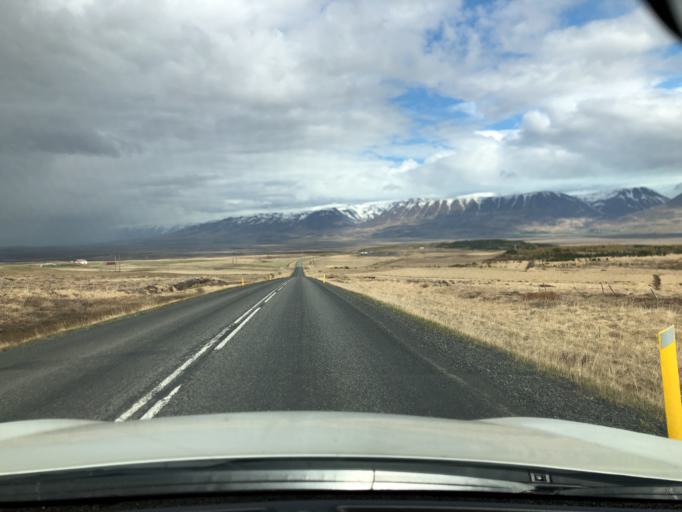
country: IS
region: Northwest
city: Saudarkrokur
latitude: 65.5408
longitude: -19.5020
